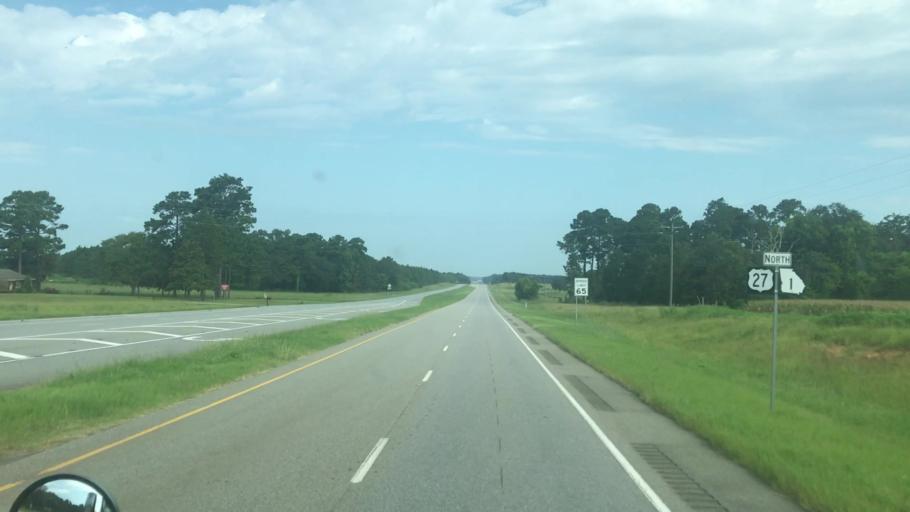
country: US
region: Georgia
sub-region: Early County
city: Blakely
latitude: 31.3213
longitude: -84.8832
